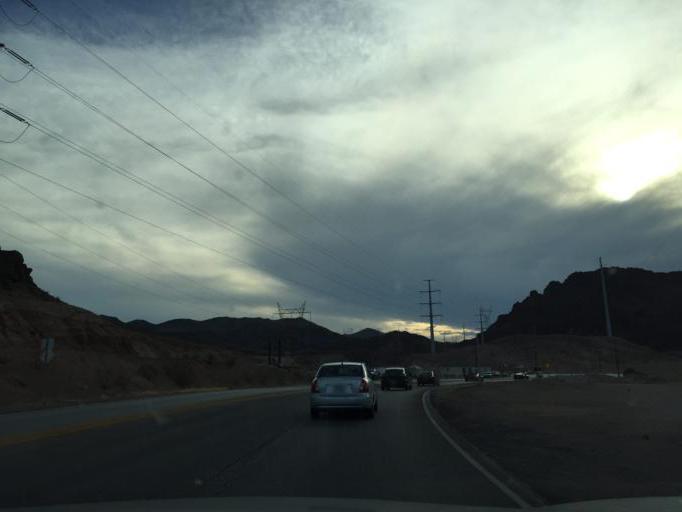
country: US
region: Nevada
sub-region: Clark County
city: Boulder City
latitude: 36.0144
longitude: -114.7528
